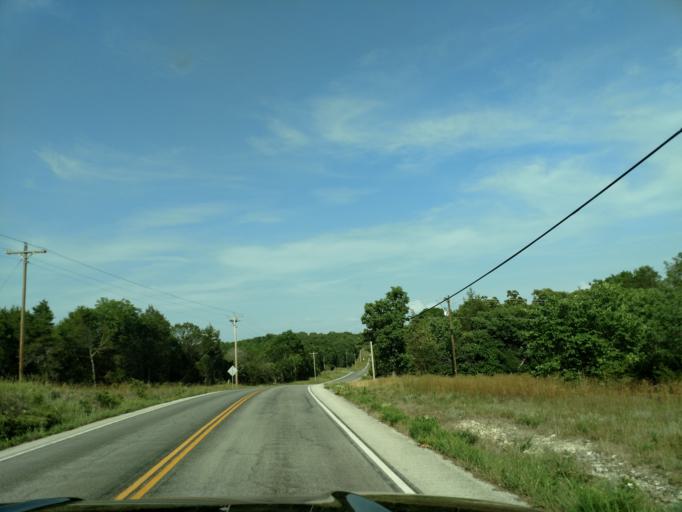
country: US
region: Missouri
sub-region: Barry County
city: Shell Knob
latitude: 36.6103
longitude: -93.5793
